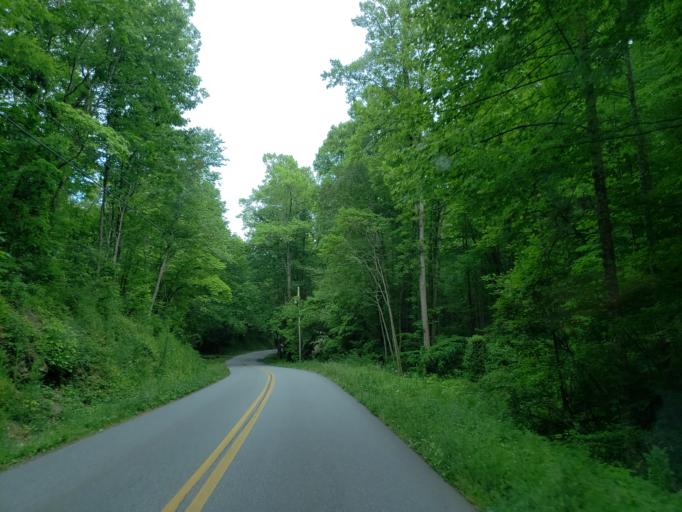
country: US
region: Georgia
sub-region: Fannin County
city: Blue Ridge
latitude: 34.8596
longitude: -84.3426
